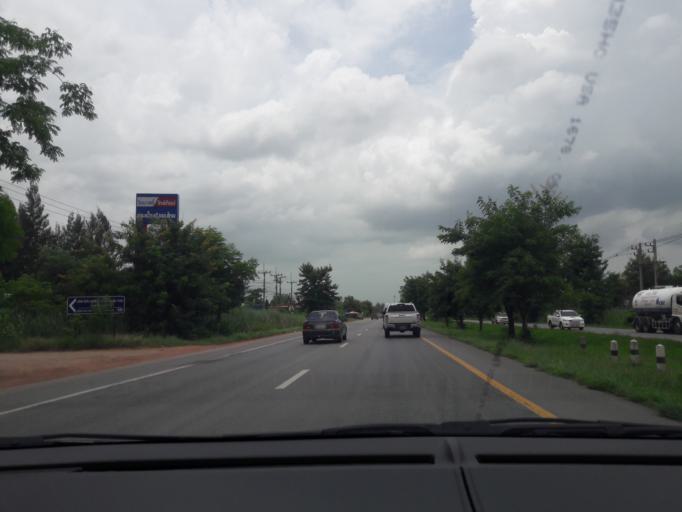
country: TH
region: Nakhon Ratchasima
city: Chaloem Phra Kiat
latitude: 15.0697
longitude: 102.2050
